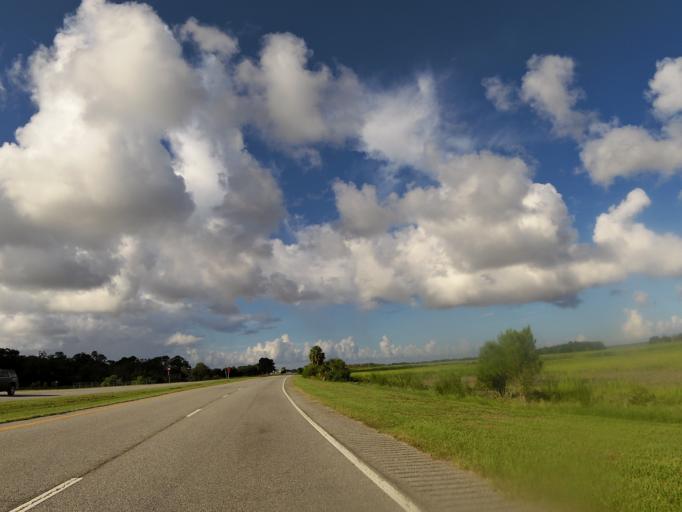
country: US
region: Georgia
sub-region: Glynn County
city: Brunswick
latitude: 31.1417
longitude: -81.4792
